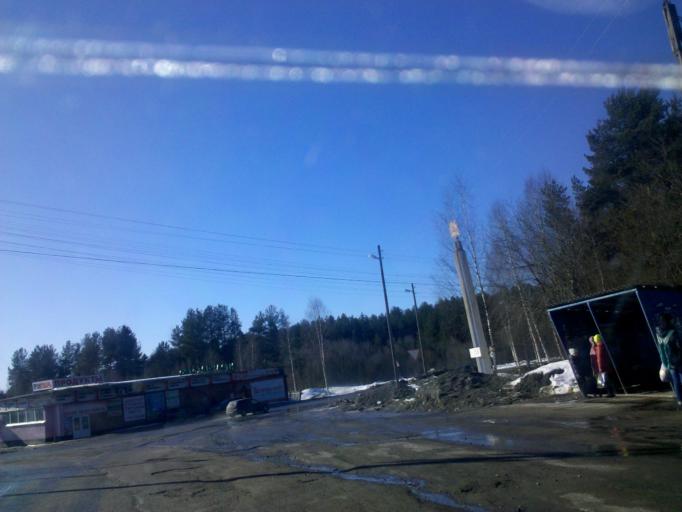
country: RU
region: Republic of Karelia
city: Pindushi
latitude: 62.9157
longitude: 34.5680
